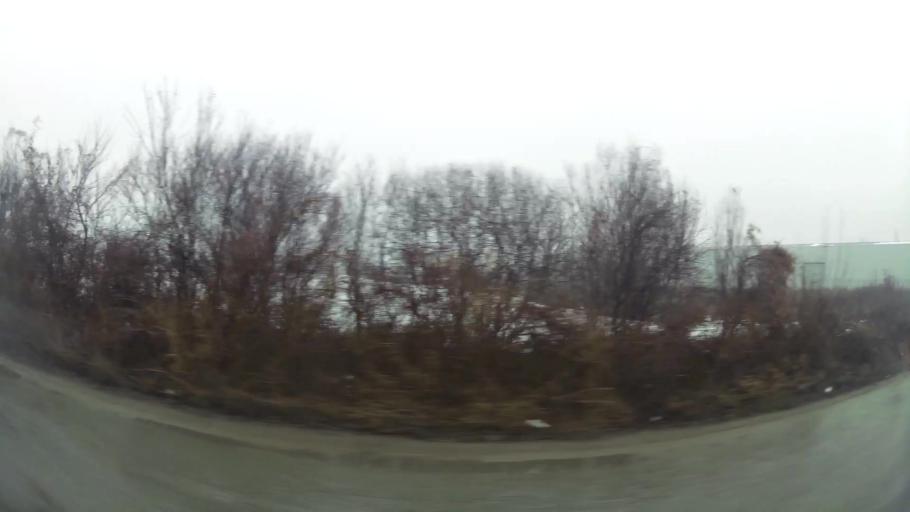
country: MK
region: Ilinden
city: Idrizovo
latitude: 41.9514
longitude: 21.5842
